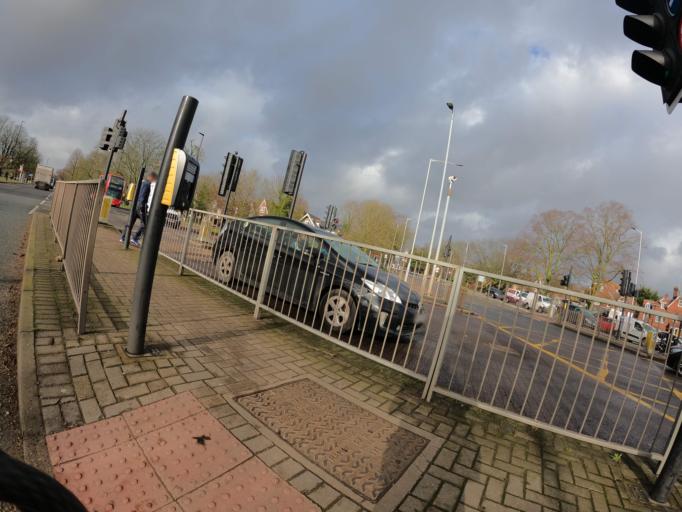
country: GB
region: England
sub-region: Greater London
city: Ealing Broadway
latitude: 51.5115
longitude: -0.2922
